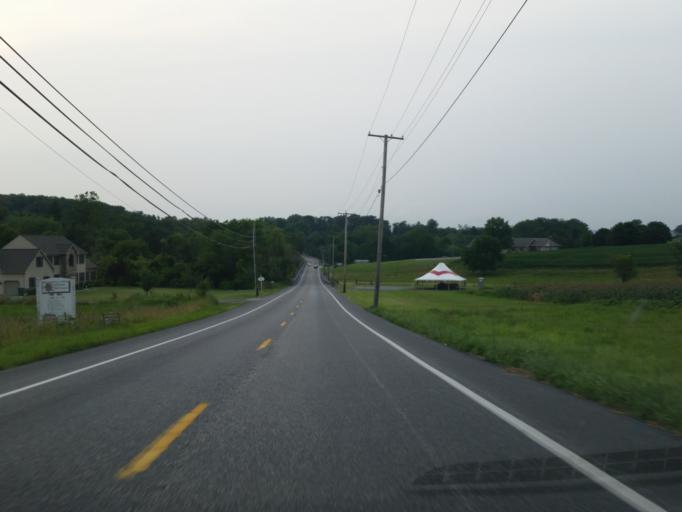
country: US
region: Pennsylvania
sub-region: Lebanon County
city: Annville
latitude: 40.3440
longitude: -76.5234
